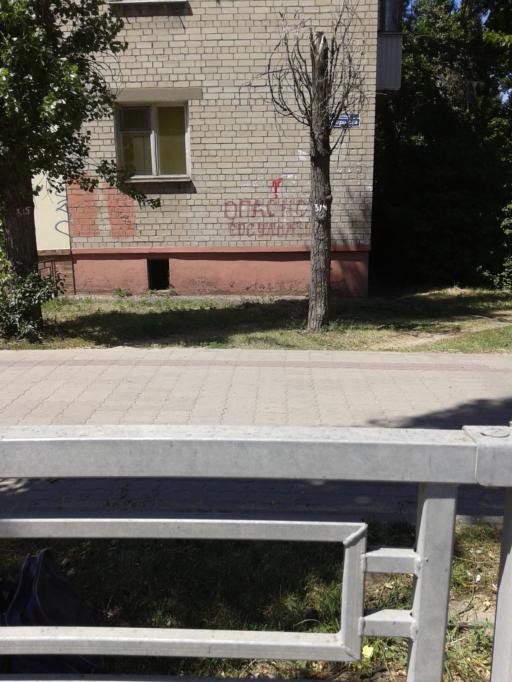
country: RU
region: Voronezj
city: Voronezh
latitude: 51.6528
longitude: 39.1458
